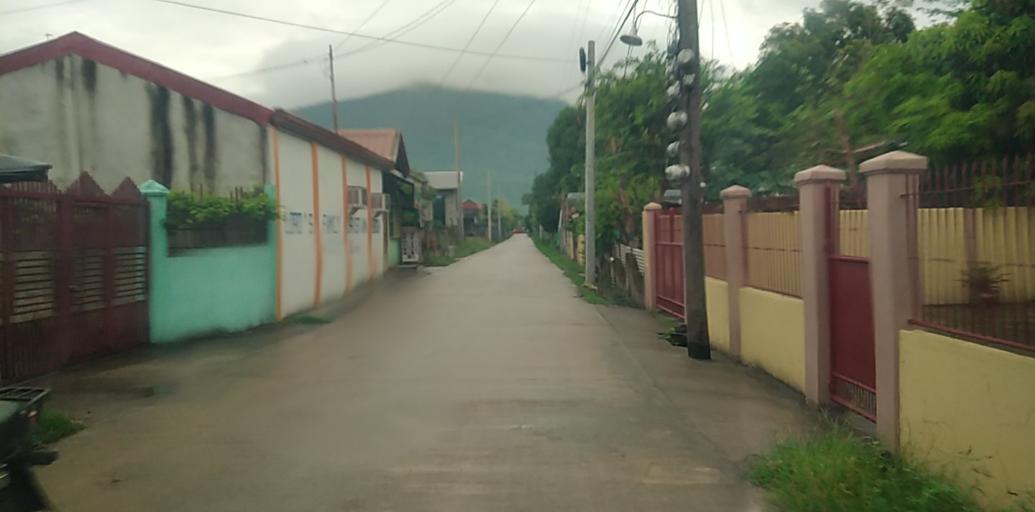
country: PH
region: Central Luzon
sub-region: Province of Pampanga
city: Anao
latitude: 15.1521
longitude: 120.7242
